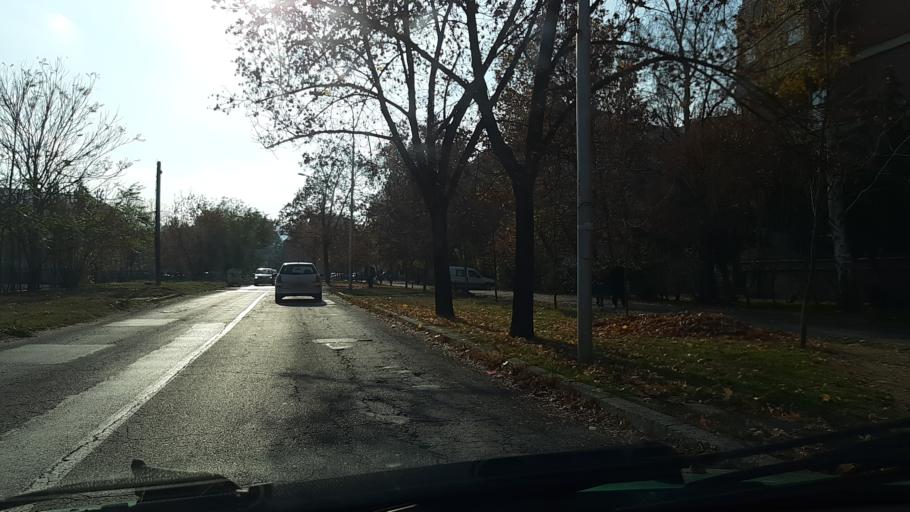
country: MK
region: Kisela Voda
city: Usje
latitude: 41.9855
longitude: 21.4602
